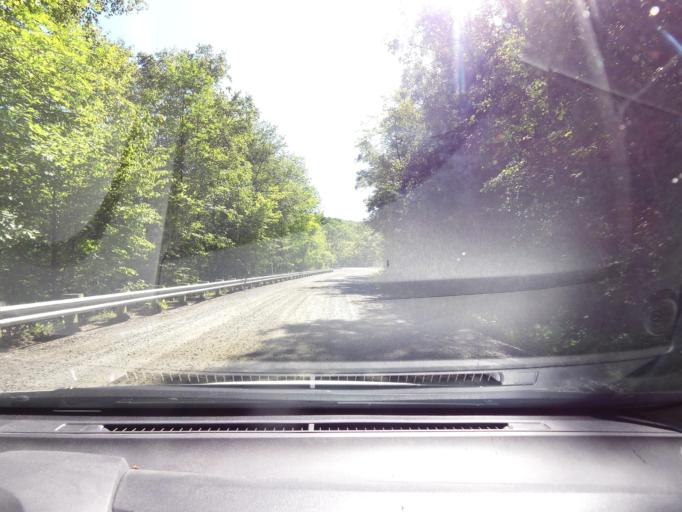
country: CA
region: Quebec
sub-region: Mauricie
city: Becancour
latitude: 46.5519
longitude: -72.4132
